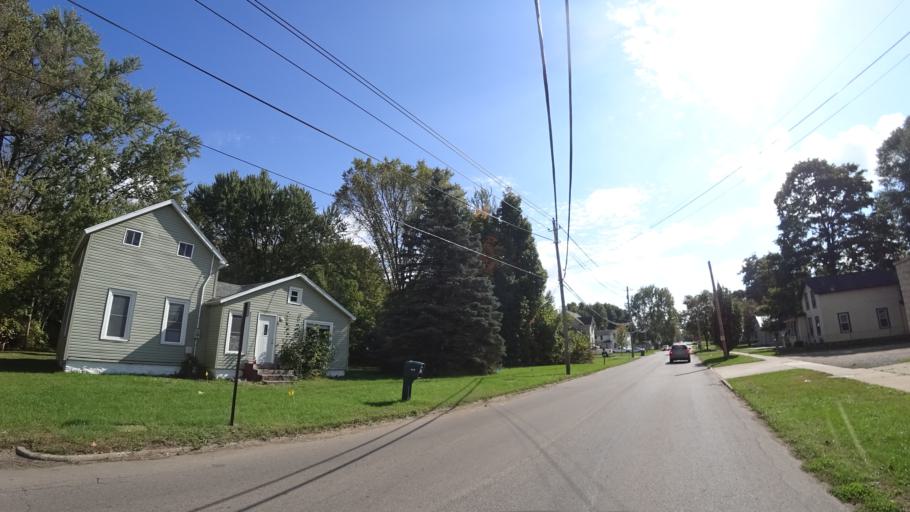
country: US
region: Michigan
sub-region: Saint Joseph County
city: Three Rivers
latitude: 41.9400
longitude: -85.6271
